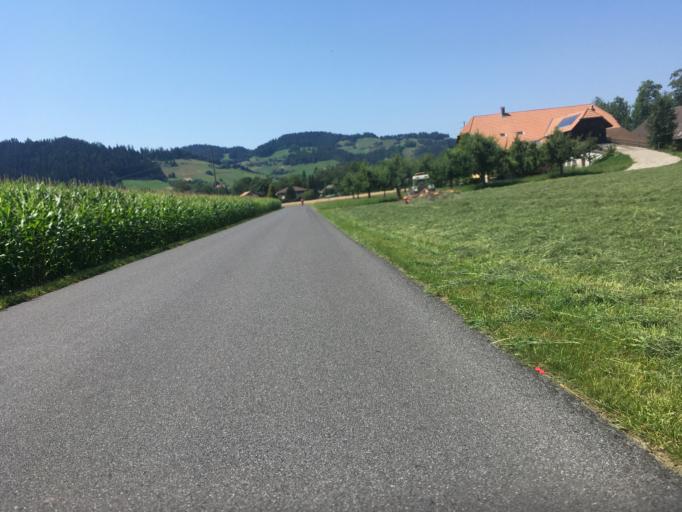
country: CH
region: Bern
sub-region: Emmental District
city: Lauperswil
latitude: 46.9473
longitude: 7.7558
